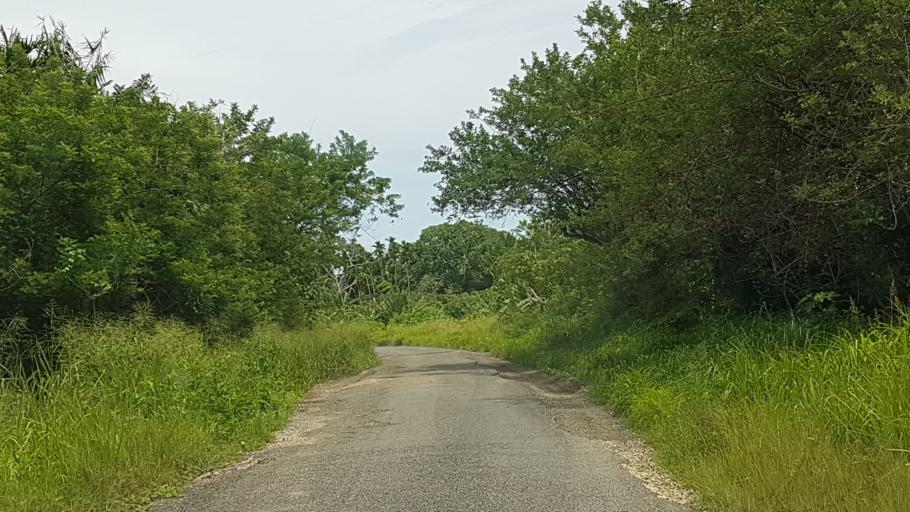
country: PG
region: Madang
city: Madang
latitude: -4.6133
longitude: 145.5547
